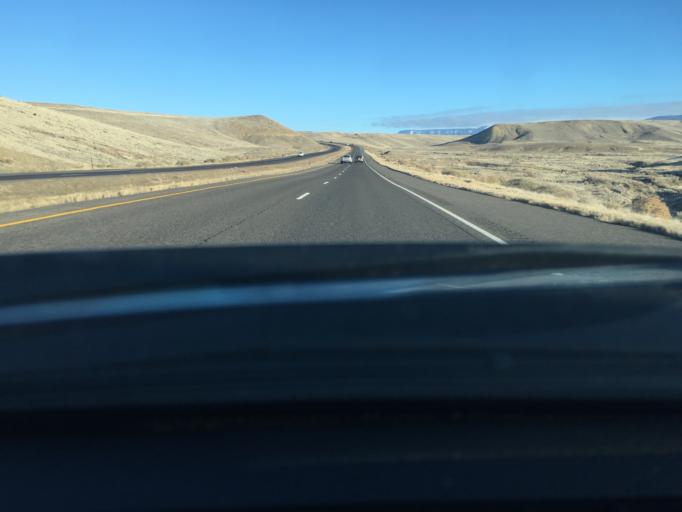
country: US
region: Colorado
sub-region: Delta County
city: Delta
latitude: 38.8339
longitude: -108.2978
